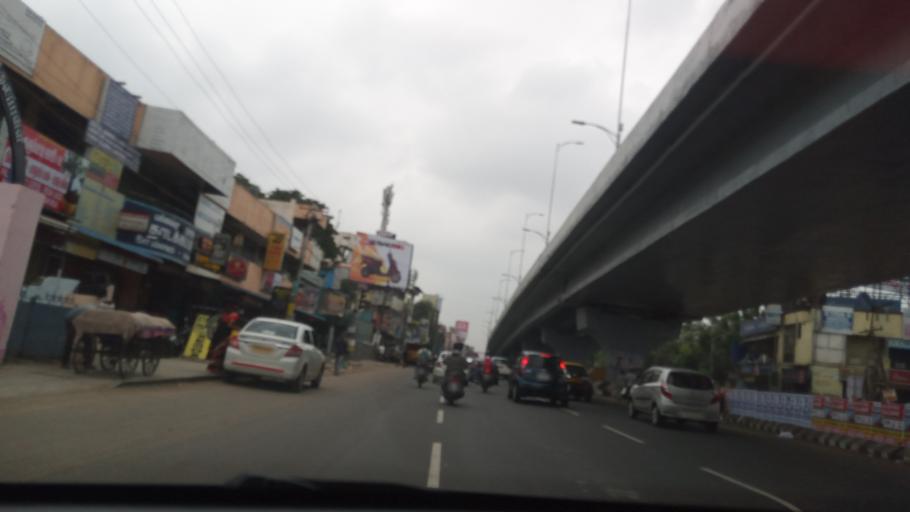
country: IN
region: Tamil Nadu
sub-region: Kancheepuram
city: Pallavaram
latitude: 12.9677
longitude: 80.1494
